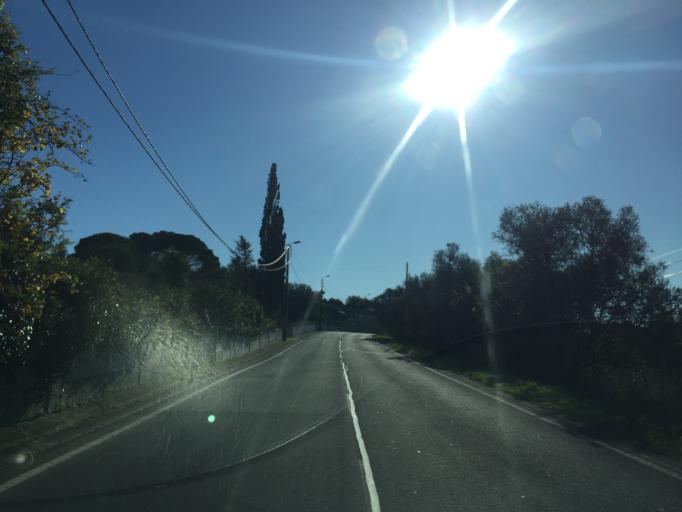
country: PT
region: Lisbon
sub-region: Sintra
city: Pero Pinheiro
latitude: 38.8371
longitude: -9.3106
